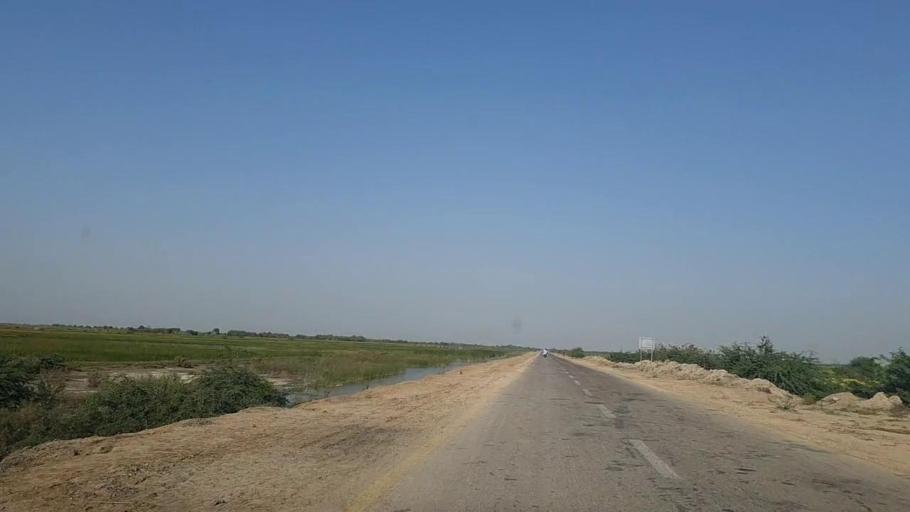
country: PK
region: Sindh
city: Jati
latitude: 24.4167
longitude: 68.3035
